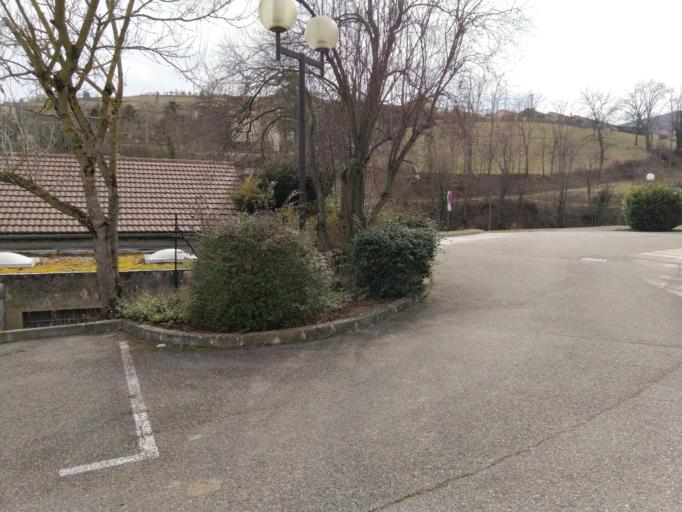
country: FR
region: Rhone-Alpes
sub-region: Departement de l'Ardeche
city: Saint-Marcel-les-Annonay
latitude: 45.2853
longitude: 4.6269
